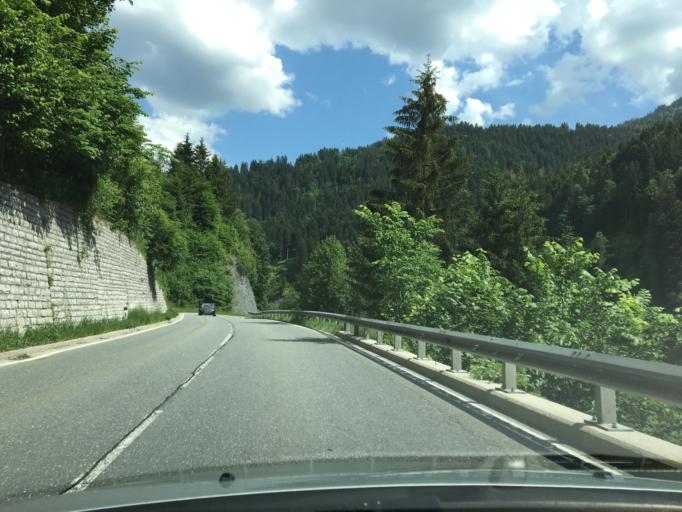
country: AT
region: Salzburg
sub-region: Politischer Bezirk Sankt Johann im Pongau
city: Sankt Johann im Pongau
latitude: 47.3319
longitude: 13.2270
